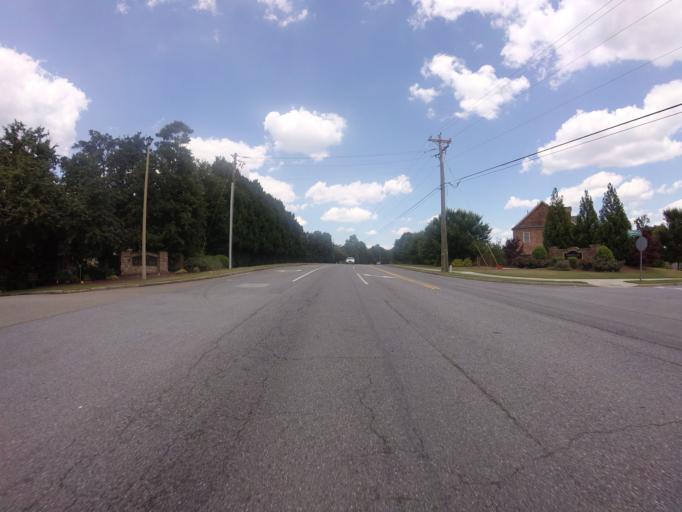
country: US
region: Georgia
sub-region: Fulton County
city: Johns Creek
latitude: 34.0342
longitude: -84.2411
